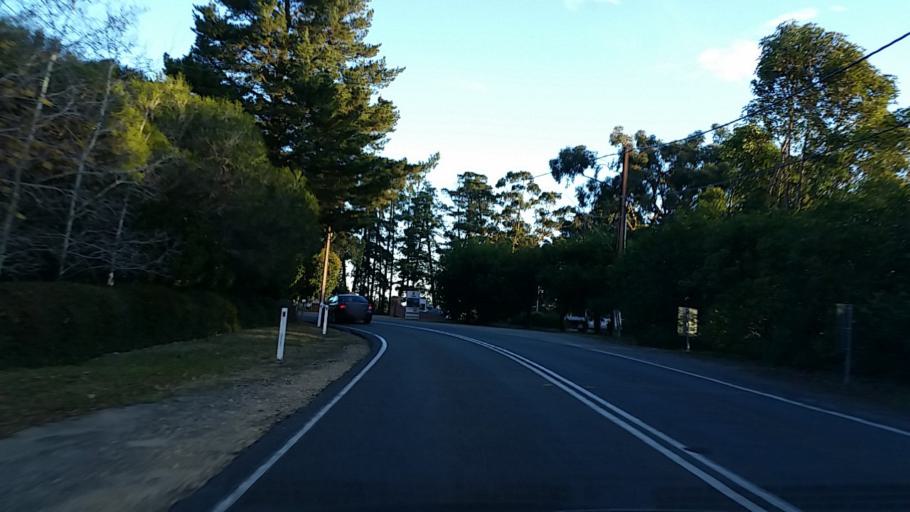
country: AU
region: South Australia
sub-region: Adelaide Hills
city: Upper Sturt
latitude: -35.0570
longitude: 138.6791
